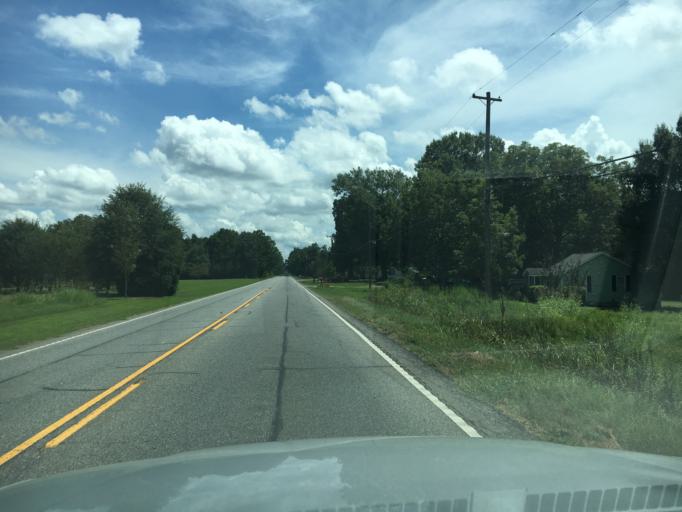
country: US
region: South Carolina
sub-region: Anderson County
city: Williamston
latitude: 34.5871
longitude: -82.4984
